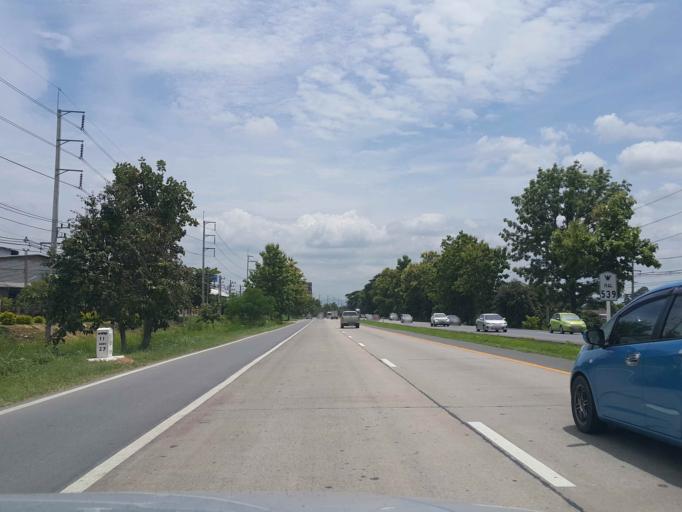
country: TH
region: Lamphun
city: Ban Thi
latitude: 18.6498
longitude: 99.0532
